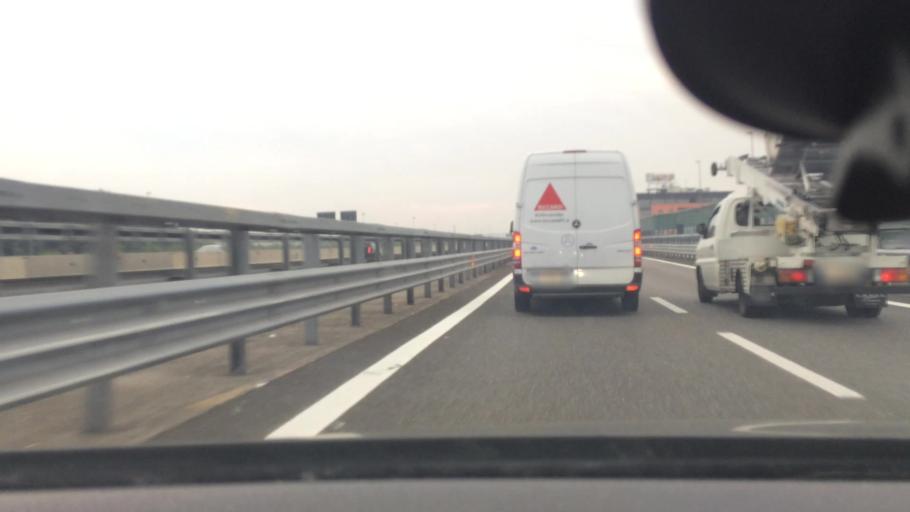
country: IT
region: Lombardy
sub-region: Citta metropolitana di Milano
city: Pero
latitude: 45.5138
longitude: 9.0882
